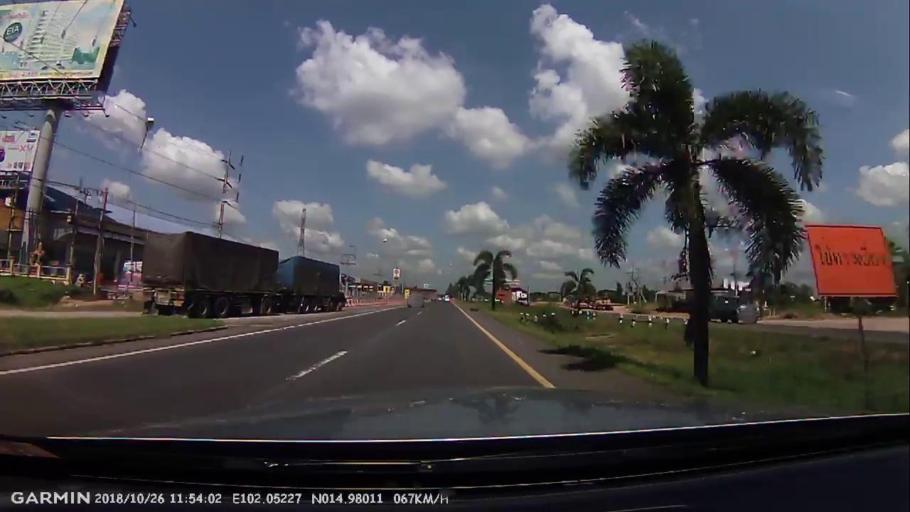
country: TH
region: Nakhon Ratchasima
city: Nakhon Ratchasima
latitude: 14.9803
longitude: 102.0523
